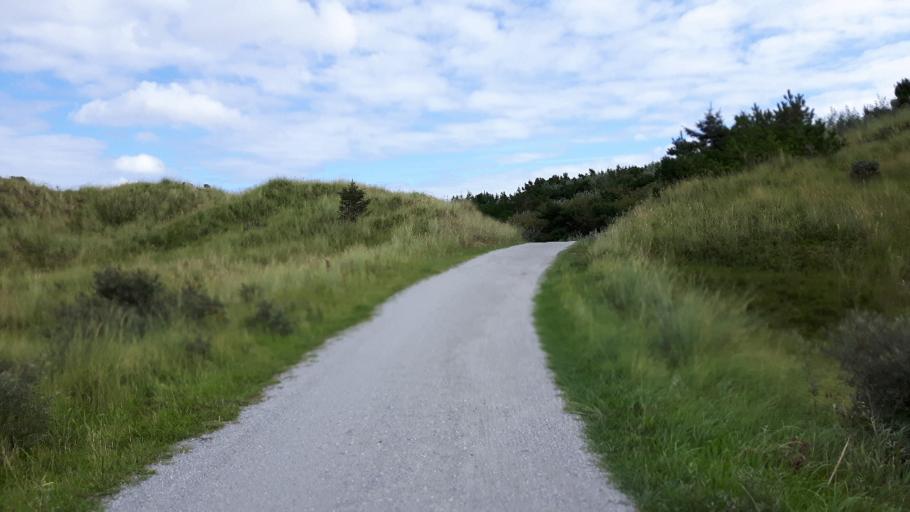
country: NL
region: Friesland
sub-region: Gemeente Ameland
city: Nes
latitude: 53.4573
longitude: 5.7604
